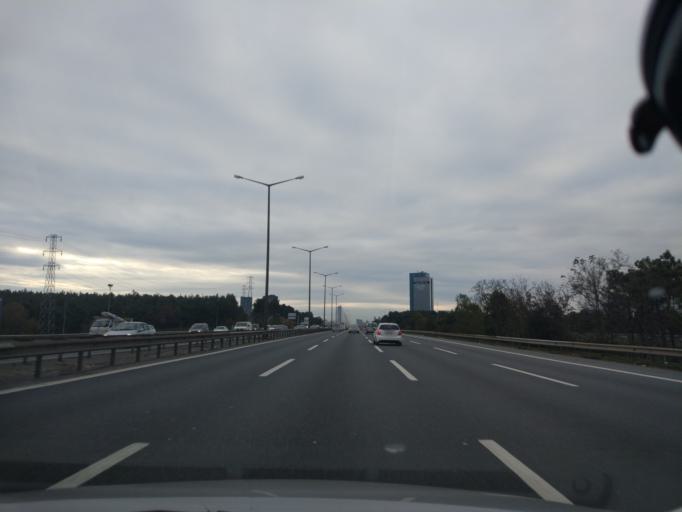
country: TR
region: Istanbul
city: Umraniye
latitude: 41.0462
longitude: 29.1209
